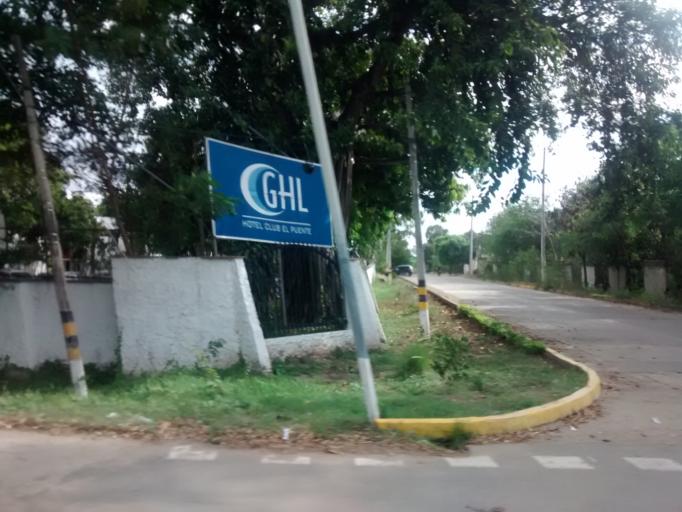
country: CO
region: Cundinamarca
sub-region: Girardot
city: Girardot City
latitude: 4.2947
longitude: -74.7854
